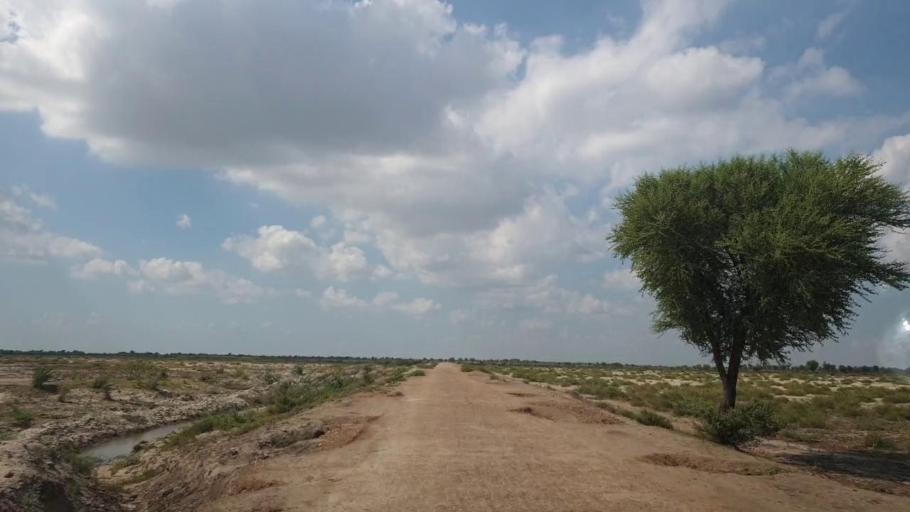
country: PK
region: Sindh
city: Pithoro
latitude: 25.5922
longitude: 69.3590
